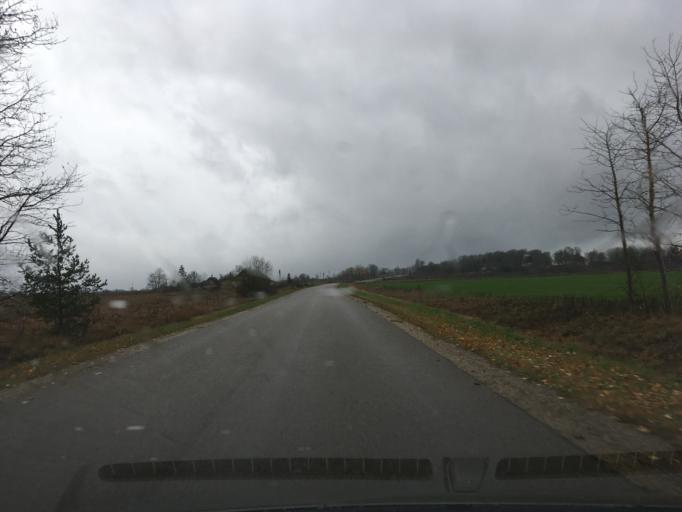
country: EE
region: Laeaene
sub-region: Lihula vald
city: Lihula
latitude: 58.6970
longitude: 23.8520
